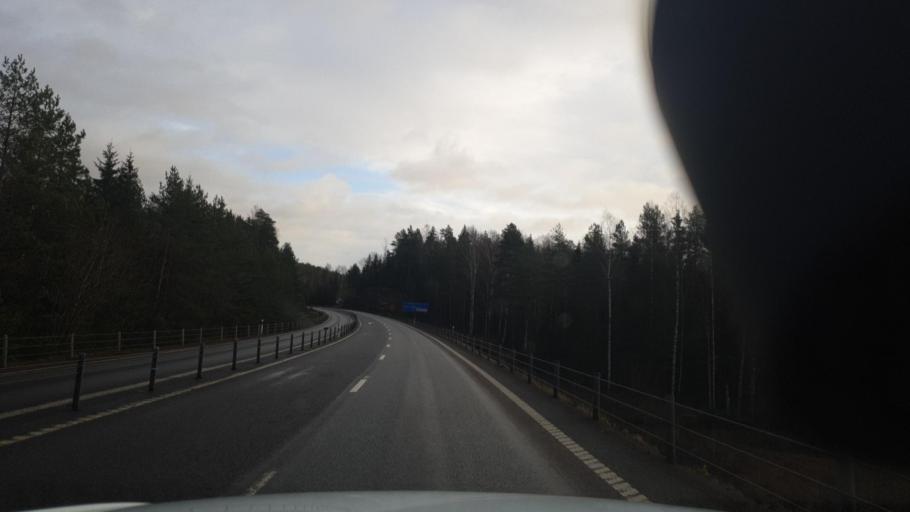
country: SE
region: Vaermland
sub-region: Arvika Kommun
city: Arvika
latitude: 59.6459
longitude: 12.7408
